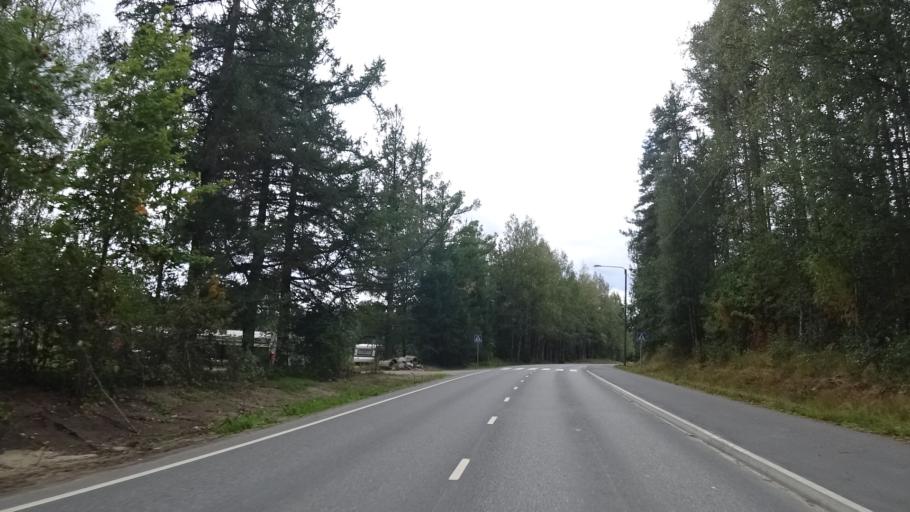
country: FI
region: North Karelia
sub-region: Joensuu
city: Ilomantsi
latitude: 62.6545
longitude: 30.9404
